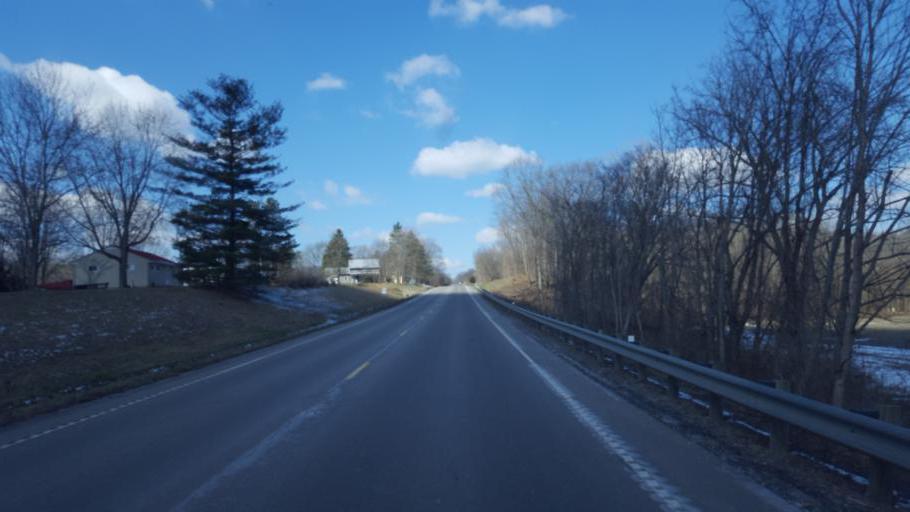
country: US
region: Ohio
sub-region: Licking County
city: Utica
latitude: 40.2299
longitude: -82.4569
